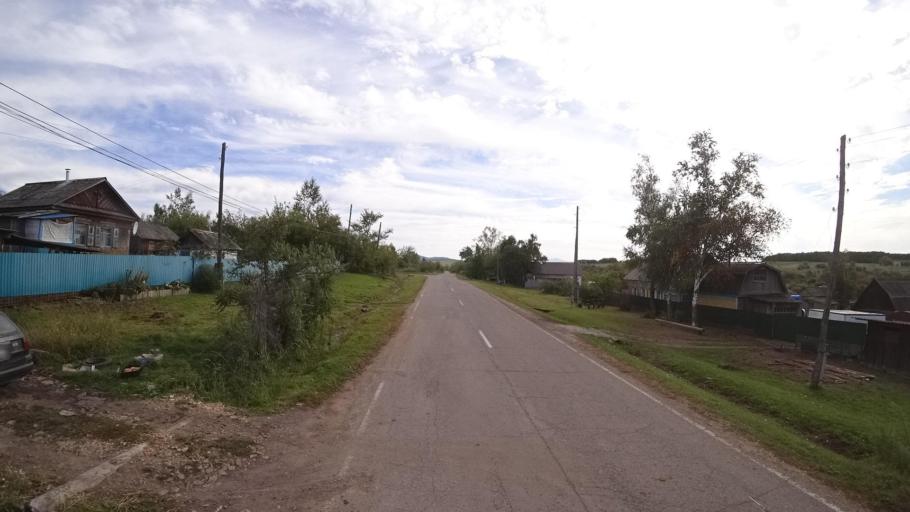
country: RU
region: Primorskiy
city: Dostoyevka
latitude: 44.3270
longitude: 133.4771
